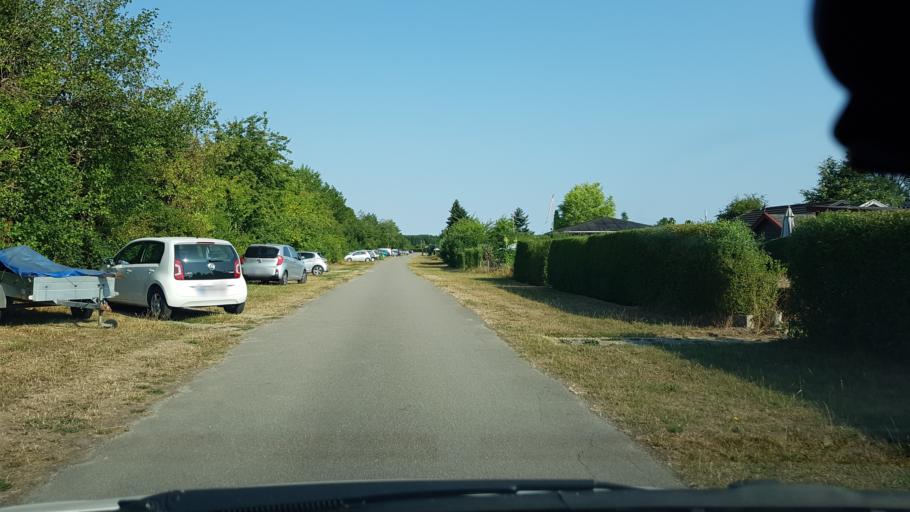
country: DK
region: Capital Region
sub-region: Vallensbaek Kommune
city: Vallensbaek
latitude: 55.6322
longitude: 12.3902
